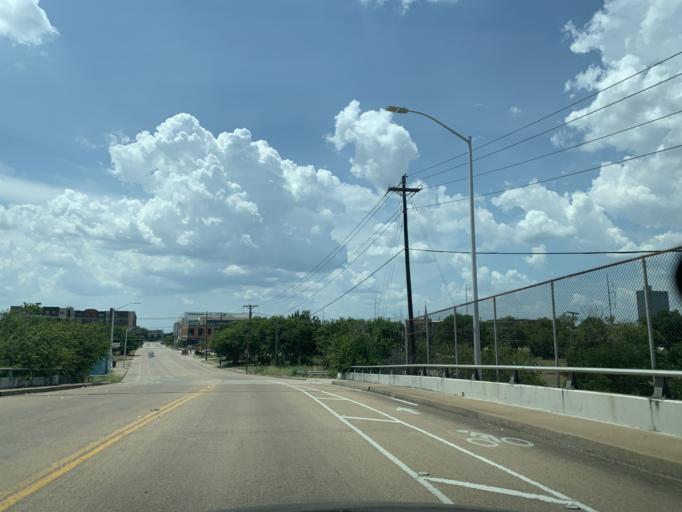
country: US
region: Texas
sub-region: Tarrant County
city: Fort Worth
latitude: 32.7379
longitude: -97.3225
